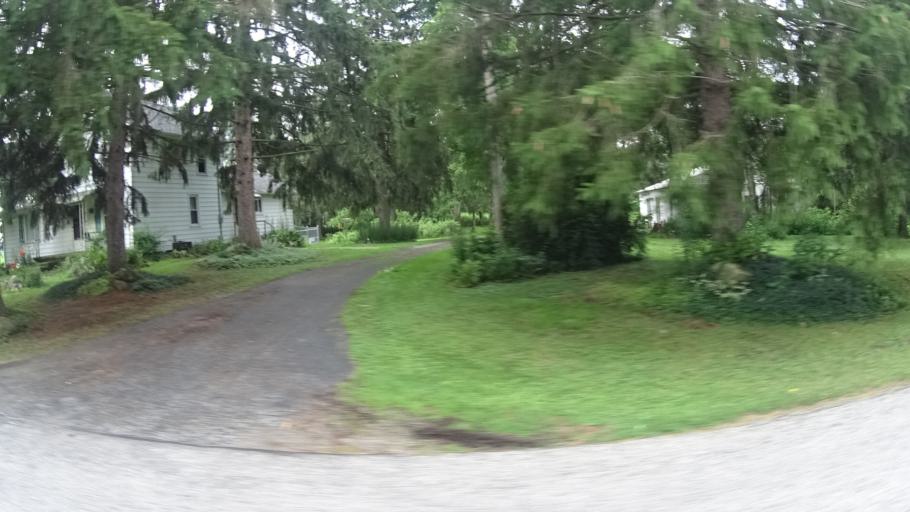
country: US
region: Ohio
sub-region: Erie County
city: Milan
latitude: 41.2993
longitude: -82.5129
